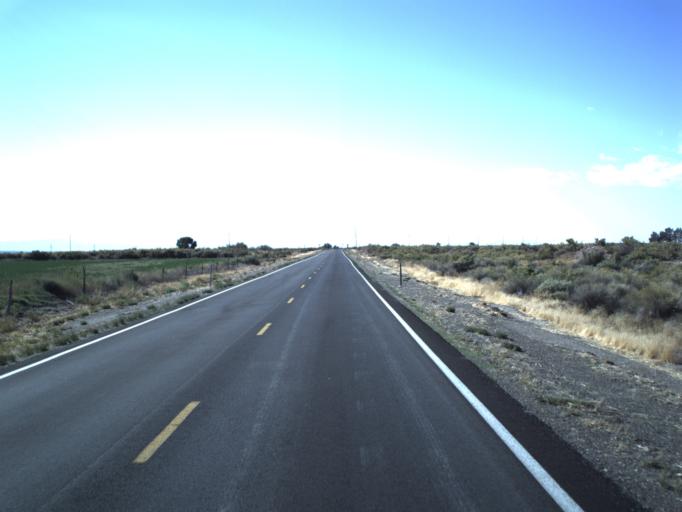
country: US
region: Utah
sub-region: Millard County
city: Delta
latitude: 39.2634
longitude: -112.6532
